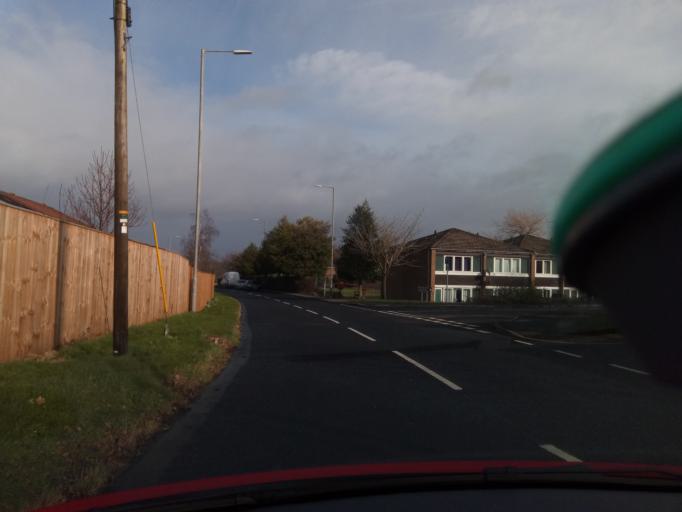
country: GB
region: Scotland
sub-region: The Scottish Borders
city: Kelso
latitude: 55.5898
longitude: -2.4364
